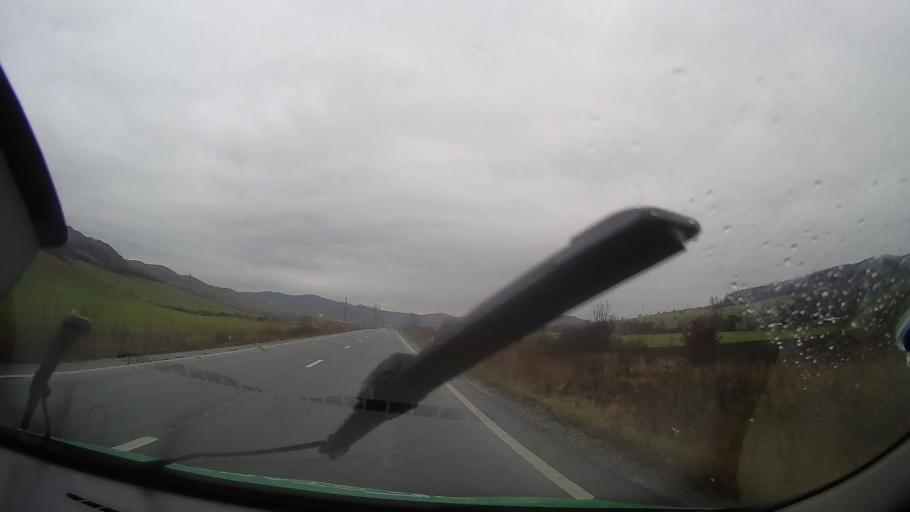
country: RO
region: Bistrita-Nasaud
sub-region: Comuna Teaca
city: Teaca
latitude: 46.9311
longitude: 24.4816
